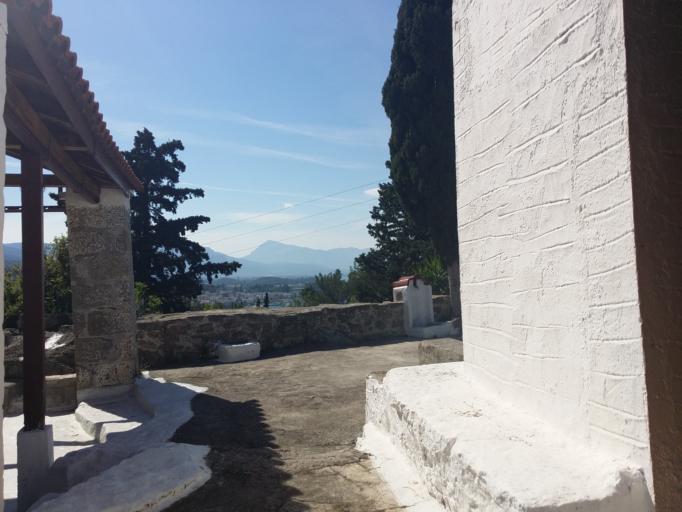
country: GR
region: Attica
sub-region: Nomos Piraios
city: Poros
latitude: 37.4952
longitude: 23.4626
